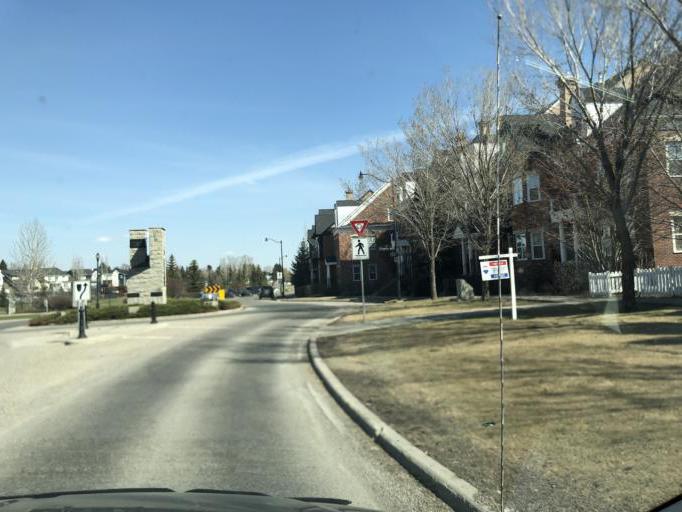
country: CA
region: Alberta
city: Calgary
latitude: 51.0161
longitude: -114.1142
